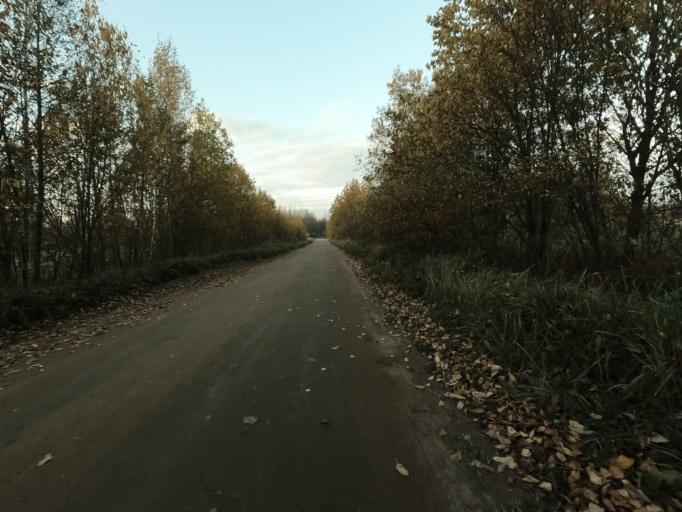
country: RU
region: Leningrad
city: Mga
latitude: 59.8048
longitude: 31.2008
